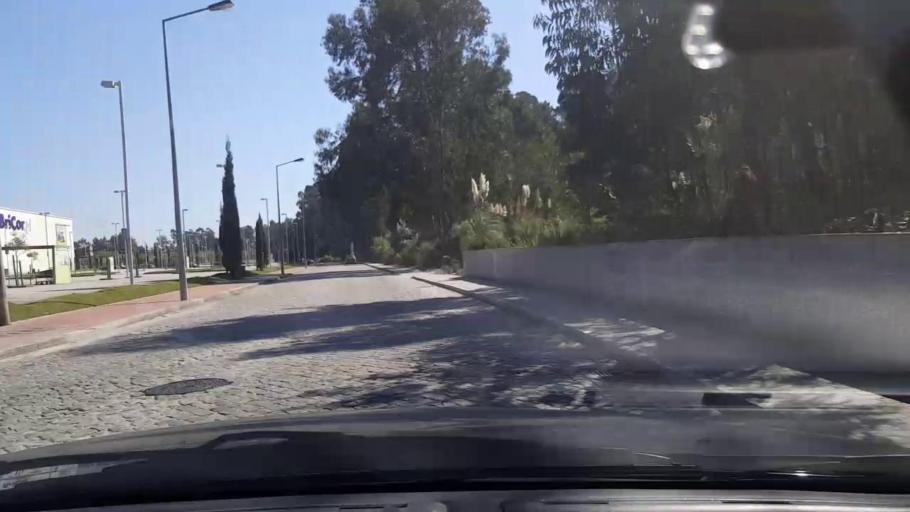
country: PT
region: Porto
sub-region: Vila do Conde
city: Arvore
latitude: 41.3004
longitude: -8.7107
